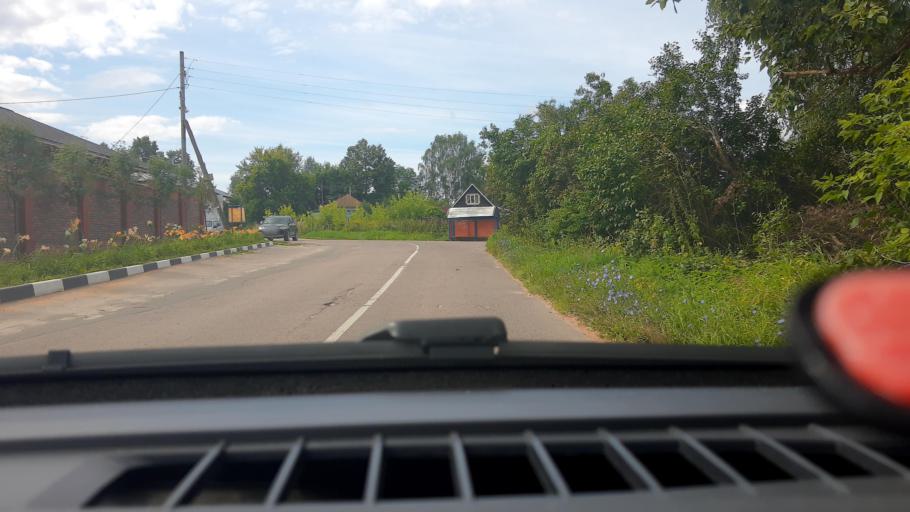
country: RU
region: Nizjnij Novgorod
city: Burevestnik
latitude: 56.0337
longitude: 43.7197
